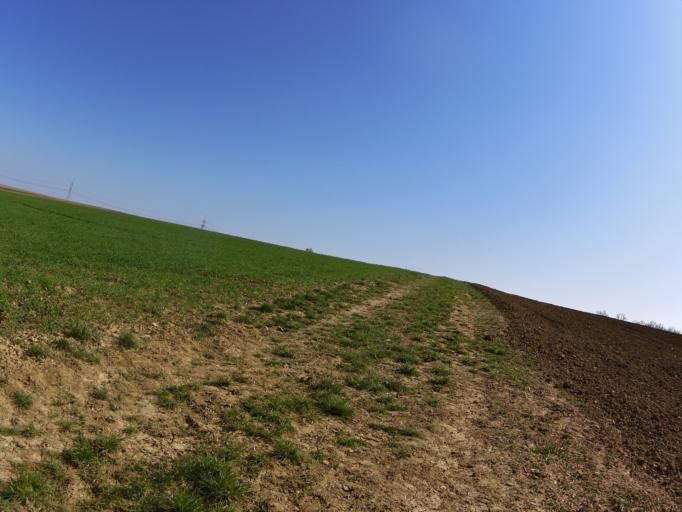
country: DE
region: Bavaria
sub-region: Regierungsbezirk Unterfranken
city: Rottendorf
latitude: 49.8198
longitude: 10.0689
